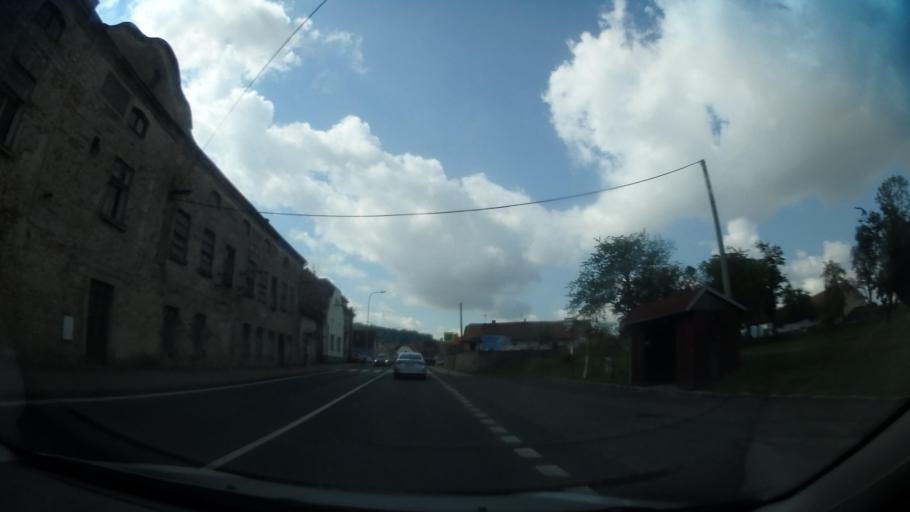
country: CZ
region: Central Bohemia
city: Cervene Pecky
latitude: 49.9466
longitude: 15.2071
